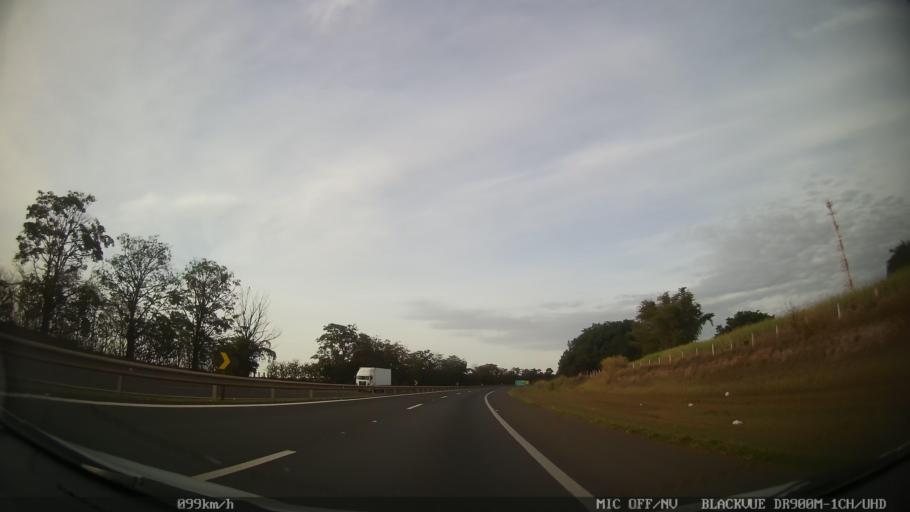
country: BR
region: Sao Paulo
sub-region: Iracemapolis
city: Iracemapolis
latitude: -22.6698
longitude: -47.5527
